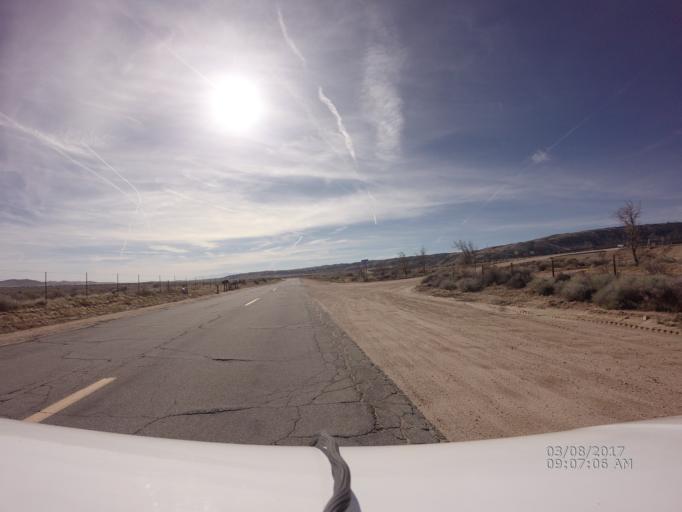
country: US
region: California
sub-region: Los Angeles County
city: Green Valley
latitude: 34.7481
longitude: -118.4868
